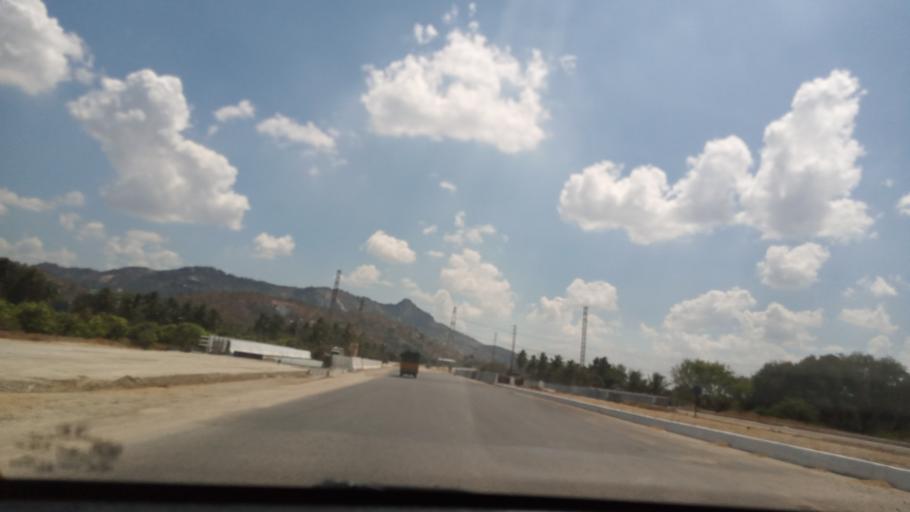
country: IN
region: Andhra Pradesh
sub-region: Chittoor
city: Pakala
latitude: 13.3460
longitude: 79.0825
